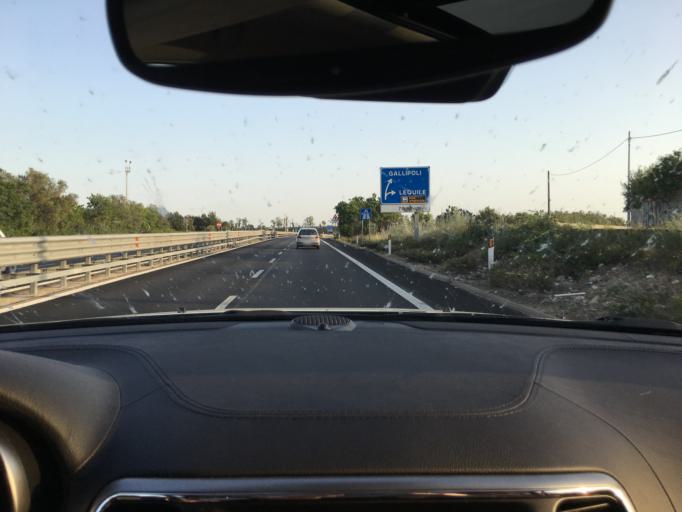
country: IT
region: Apulia
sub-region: Provincia di Lecce
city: Lequile
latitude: 40.2931
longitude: 18.1327
